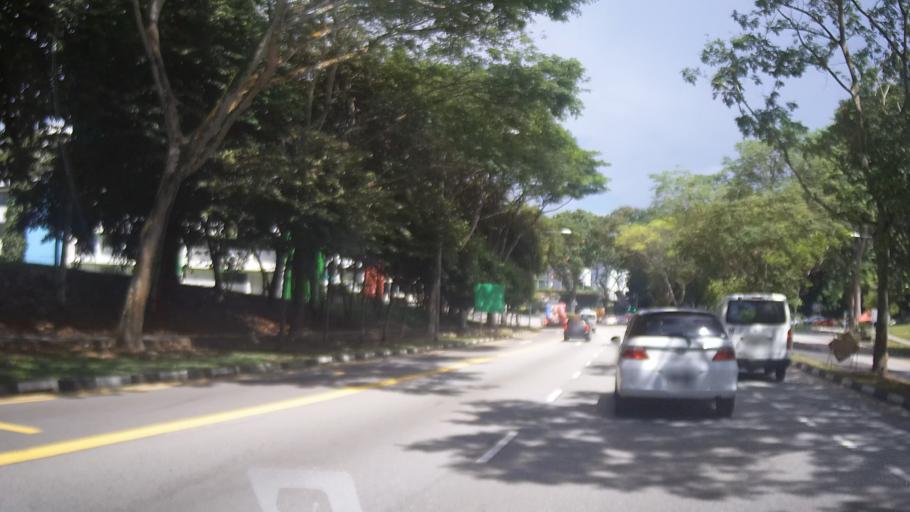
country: SG
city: Singapore
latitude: 1.3502
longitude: 103.7702
